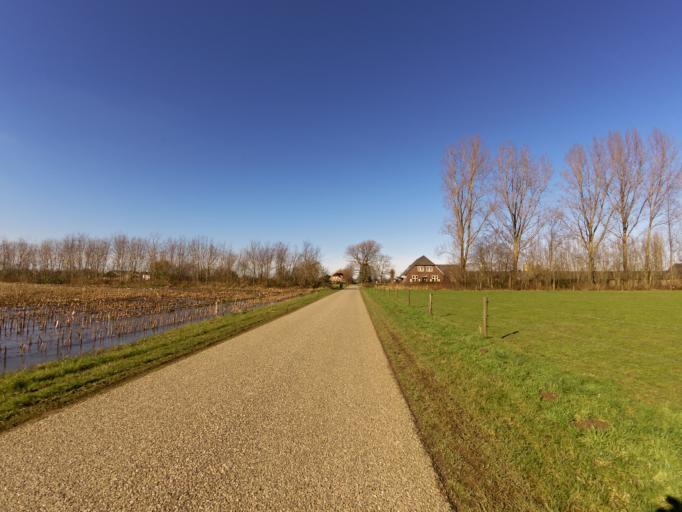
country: NL
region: Gelderland
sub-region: Gemeente Doetinchem
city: Doetinchem
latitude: 51.9604
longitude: 6.2388
